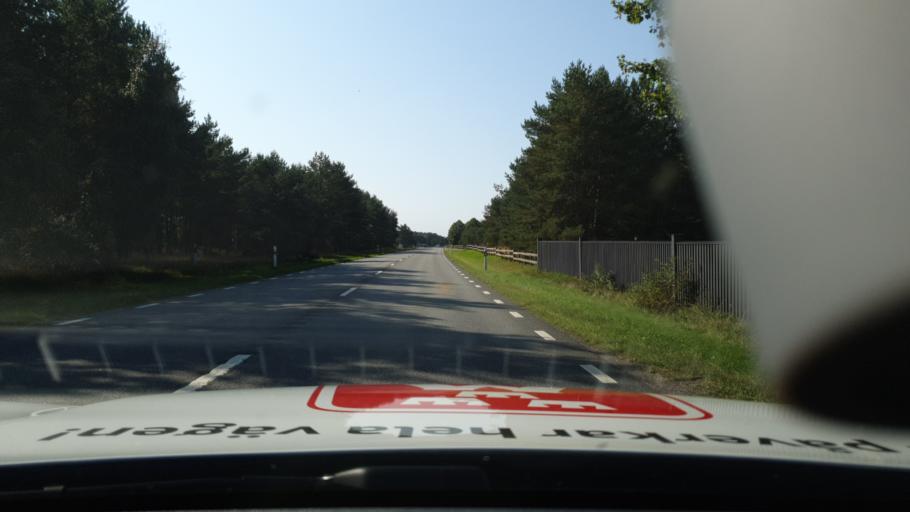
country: SE
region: Skane
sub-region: Kristianstads Kommun
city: Ahus
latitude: 55.8961
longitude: 14.2524
